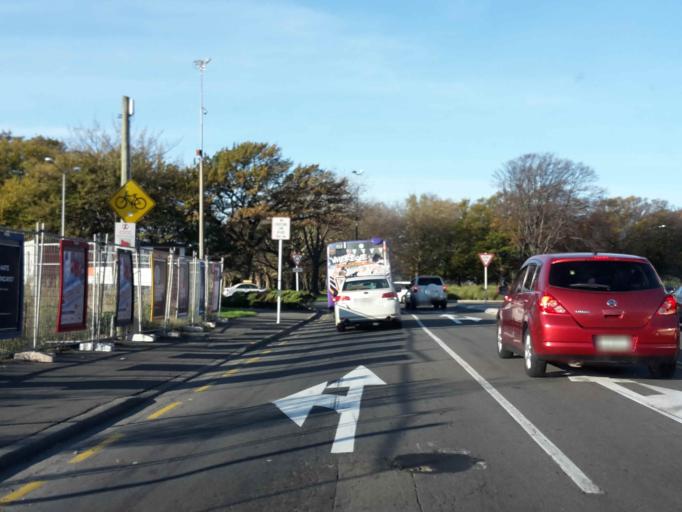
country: NZ
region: Canterbury
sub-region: Christchurch City
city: Christchurch
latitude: -43.5288
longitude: 172.6115
